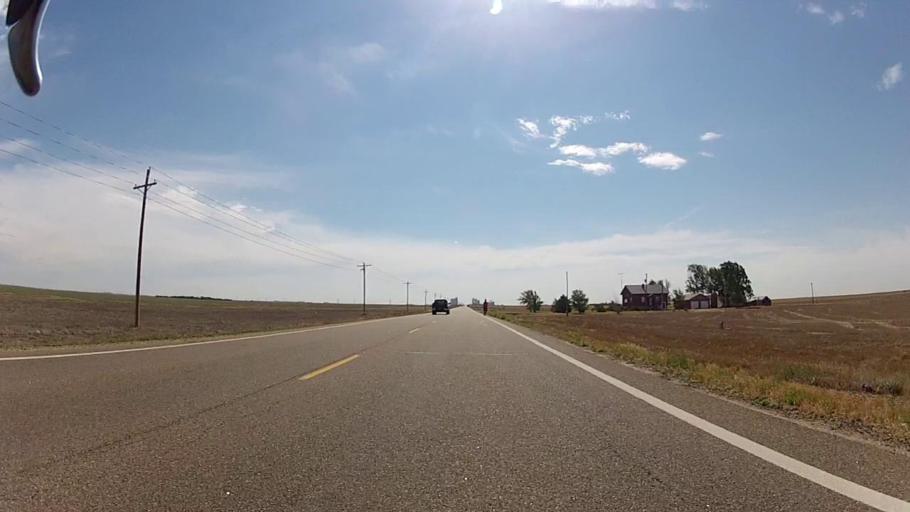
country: US
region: Kansas
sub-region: Grant County
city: Ulysses
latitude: 37.5616
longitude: -101.2659
